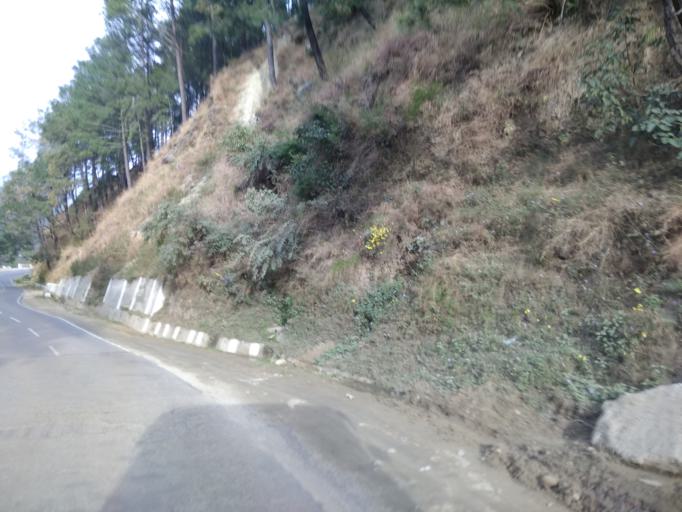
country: IN
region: Himachal Pradesh
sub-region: Kangra
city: Palampur
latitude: 32.1105
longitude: 76.4907
